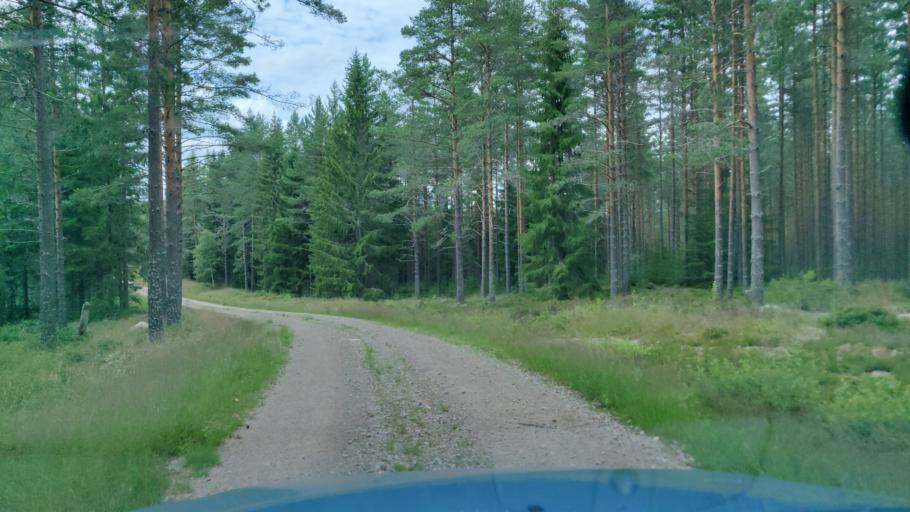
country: SE
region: Vaermland
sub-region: Hagfors Kommun
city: Hagfors
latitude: 59.9503
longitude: 13.5933
